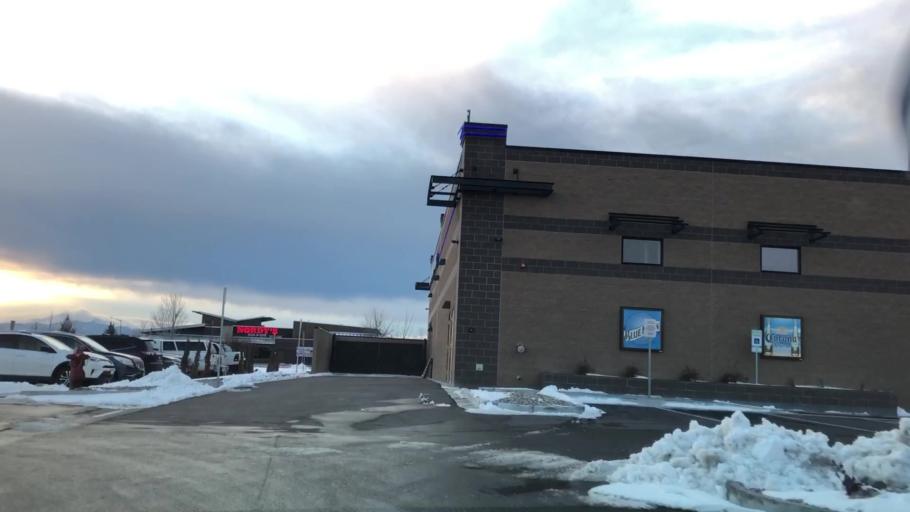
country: US
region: Colorado
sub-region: Weld County
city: Windsor
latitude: 40.4369
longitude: -104.9815
